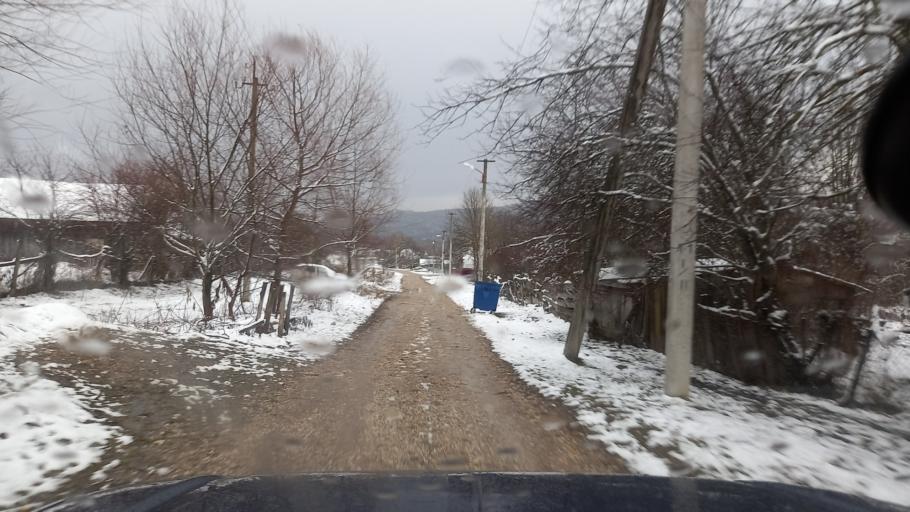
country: RU
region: Adygeya
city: Abadzekhskaya
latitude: 44.3590
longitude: 40.4108
